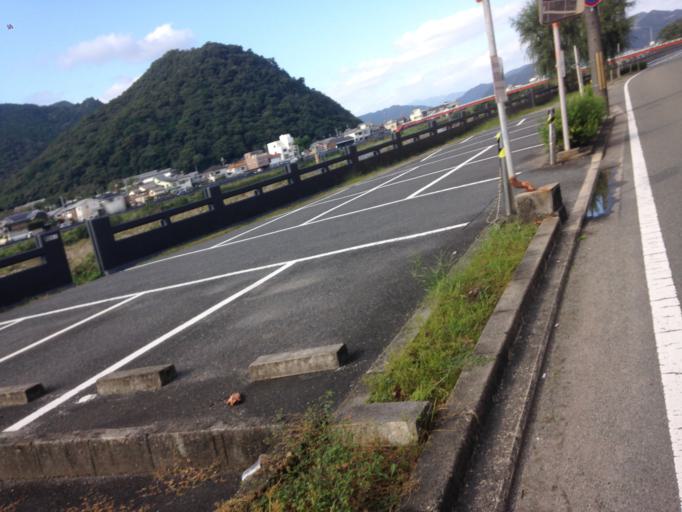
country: JP
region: Hyogo
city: Tatsunocho-tominaga
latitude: 34.8635
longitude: 134.5491
